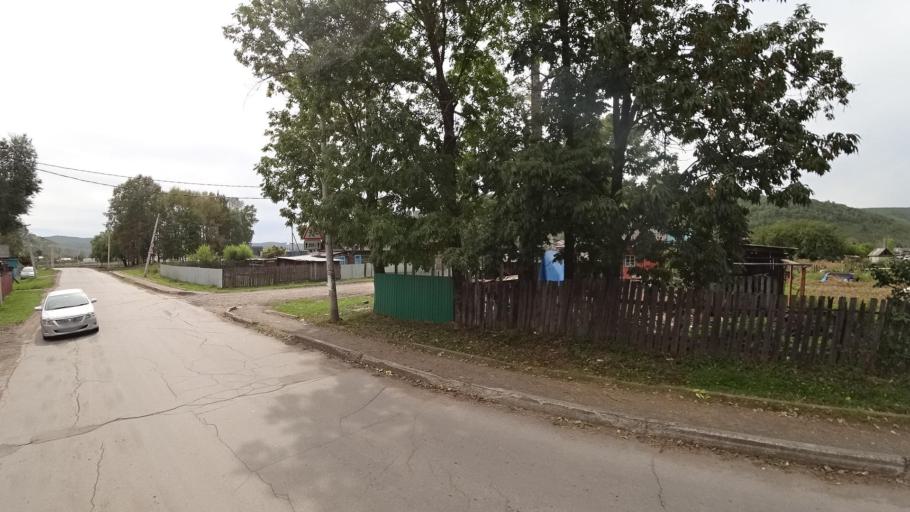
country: RU
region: Jewish Autonomous Oblast
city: Khingansk
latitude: 49.0052
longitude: 131.0537
